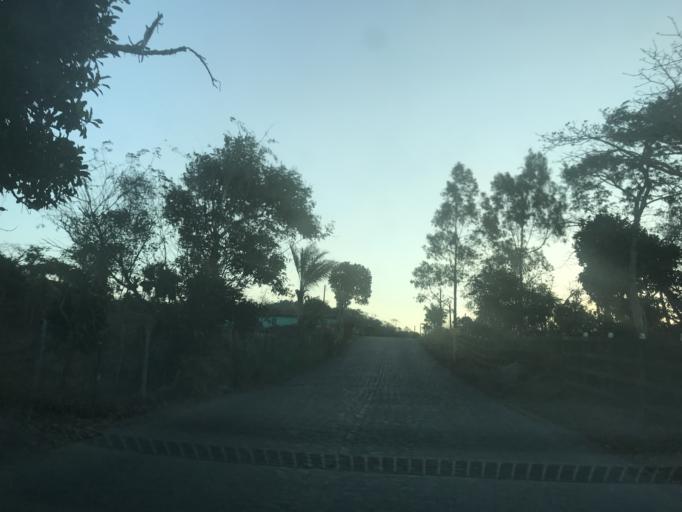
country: BR
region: Pernambuco
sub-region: Bezerros
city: Bezerros
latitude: -8.1828
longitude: -35.7614
